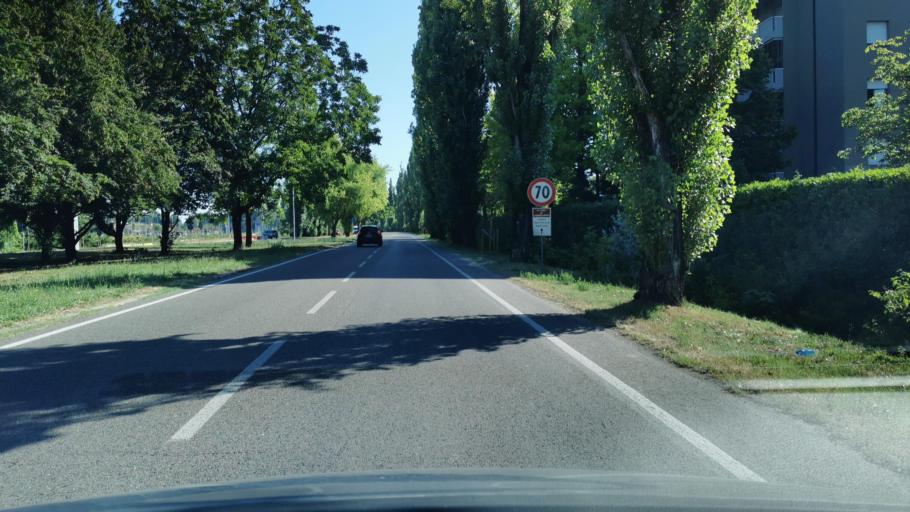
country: IT
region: Emilia-Romagna
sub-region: Provincia di Modena
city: Carpi Centro
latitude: 44.7763
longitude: 10.8635
